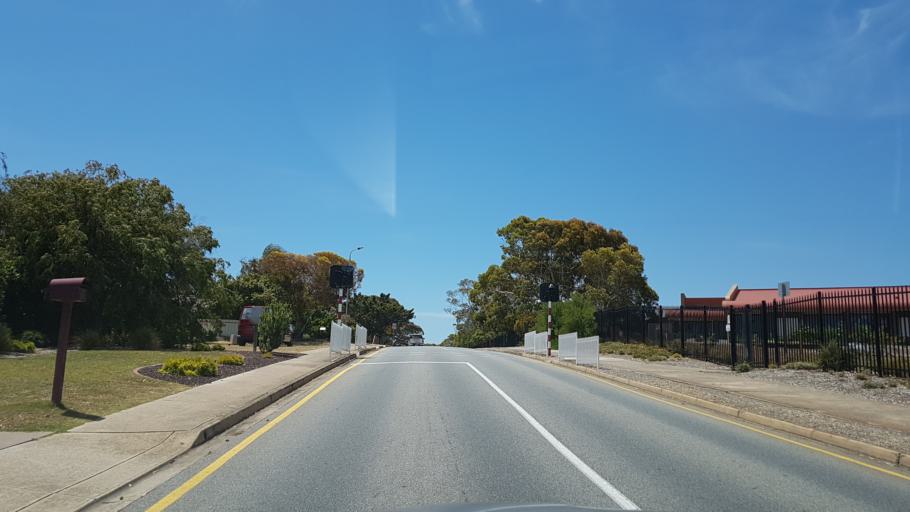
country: AU
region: South Australia
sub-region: Marion
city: Happy Valley
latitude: -35.0772
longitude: 138.5096
